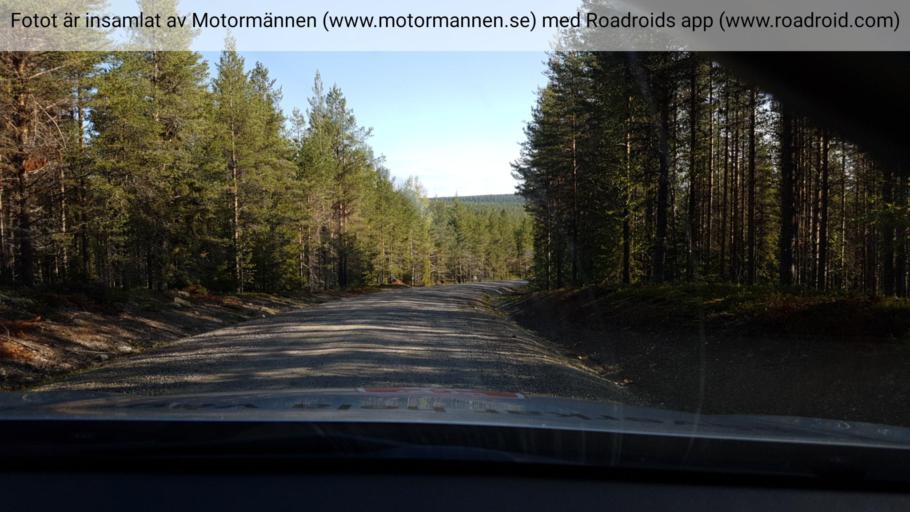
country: SE
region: Vaesterbotten
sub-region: Norsjo Kommun
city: Norsjoe
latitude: 64.6961
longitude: 19.4436
